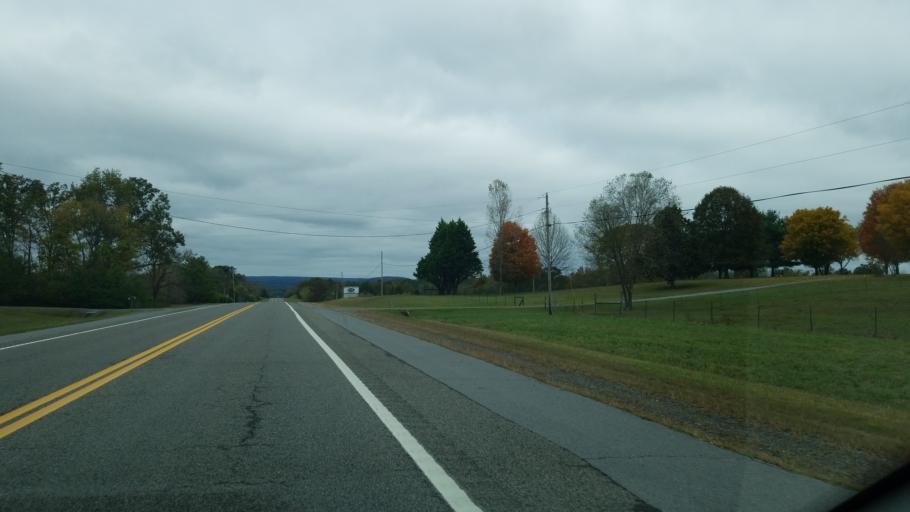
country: US
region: Tennessee
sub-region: Rhea County
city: Graysville
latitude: 35.3881
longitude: -85.0052
